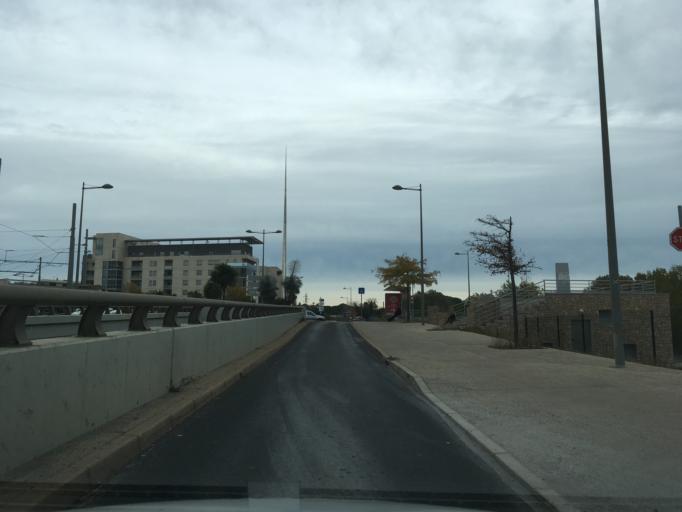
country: FR
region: Languedoc-Roussillon
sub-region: Departement de l'Herault
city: Castelnau-le-Lez
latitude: 43.6284
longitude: 3.8961
